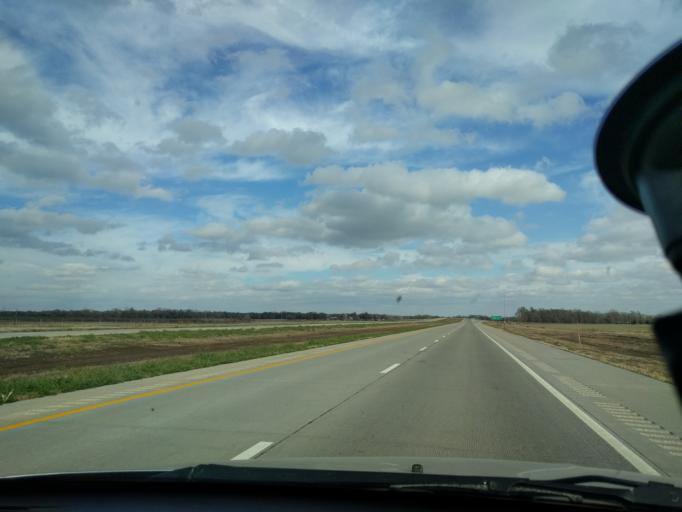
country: US
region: Kansas
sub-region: Reno County
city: Buhler
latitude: 38.1498
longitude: -97.8573
